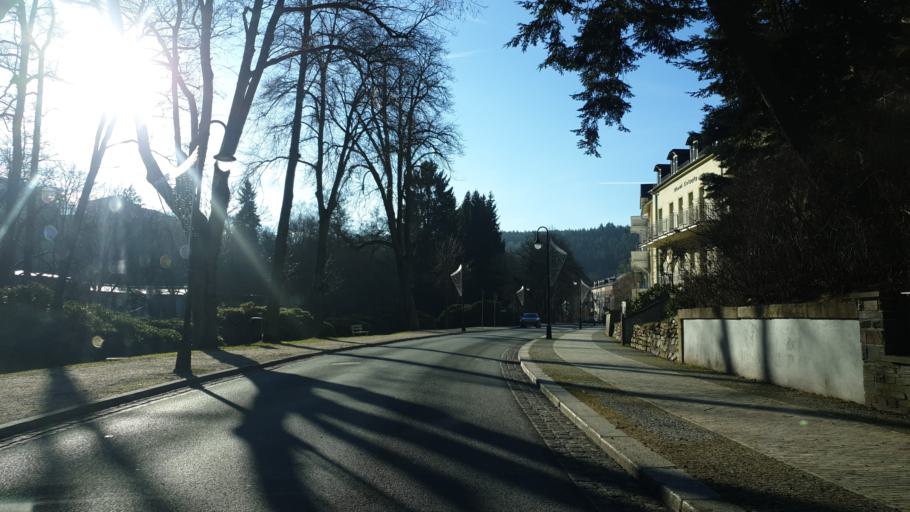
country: DE
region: Saxony
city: Bad Elster
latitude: 50.2817
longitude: 12.2395
